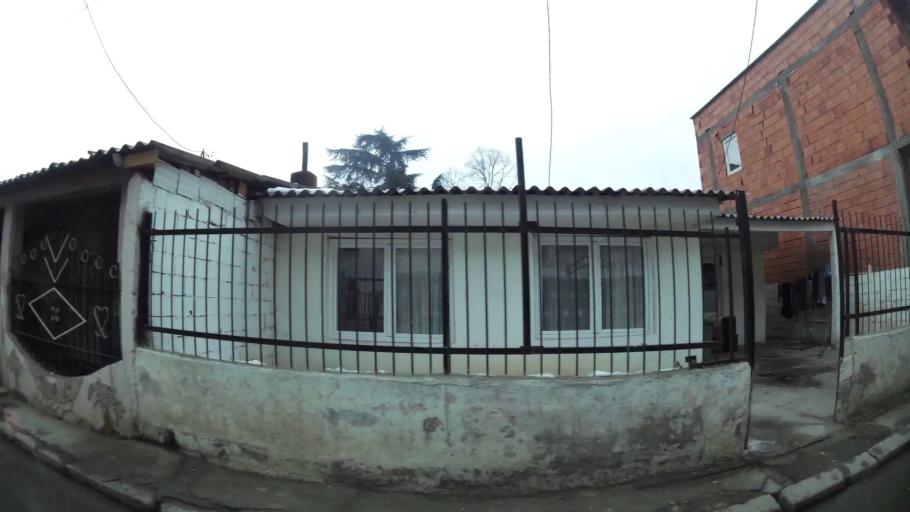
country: MK
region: Suto Orizari
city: Suto Orizare
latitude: 42.0441
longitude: 21.4268
